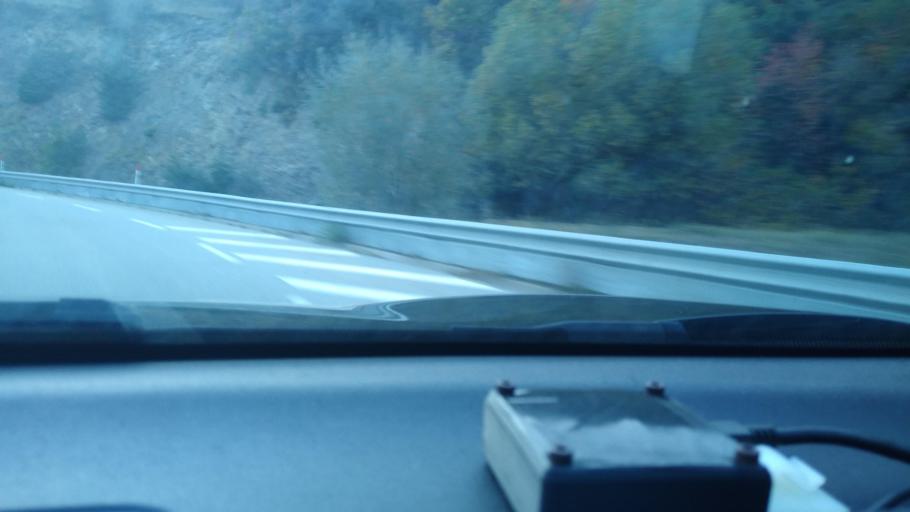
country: FR
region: Languedoc-Roussillon
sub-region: Departement des Pyrenees-Orientales
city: Vernet-les-Bains
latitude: 42.5197
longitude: 2.2044
